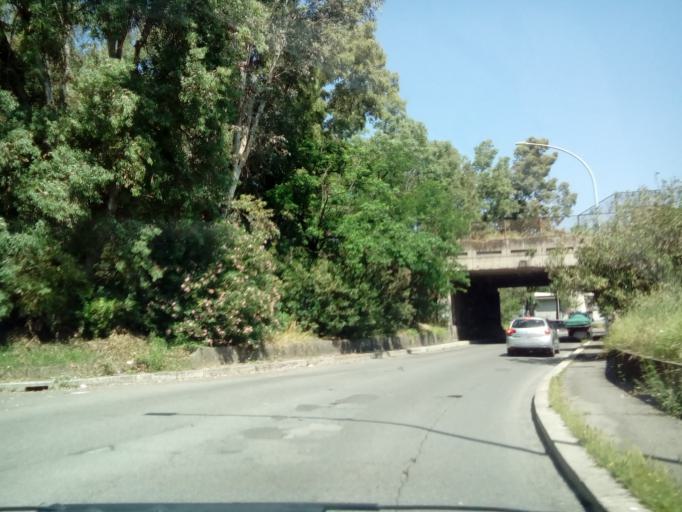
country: IT
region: Latium
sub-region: Citta metropolitana di Roma Capitale
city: Rome
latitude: 41.8866
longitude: 12.5859
